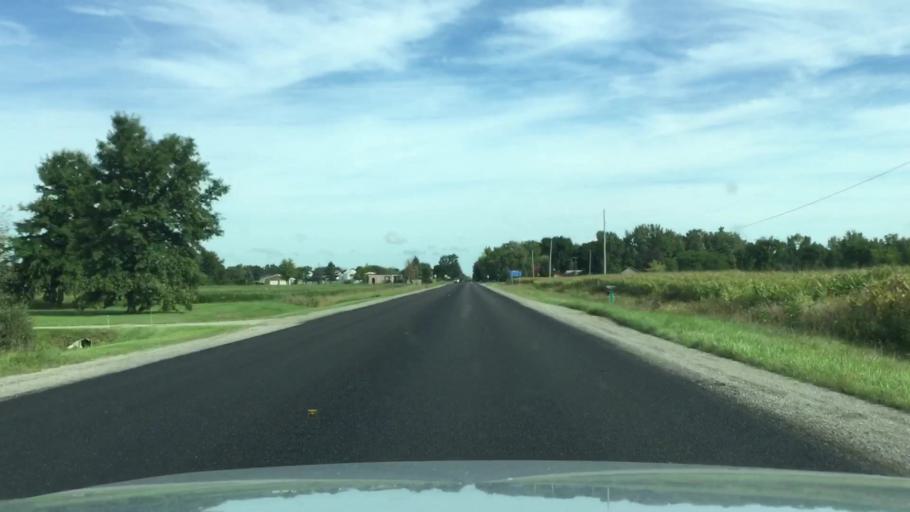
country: US
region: Michigan
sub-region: Genesee County
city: Montrose
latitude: 43.1443
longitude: -83.9295
